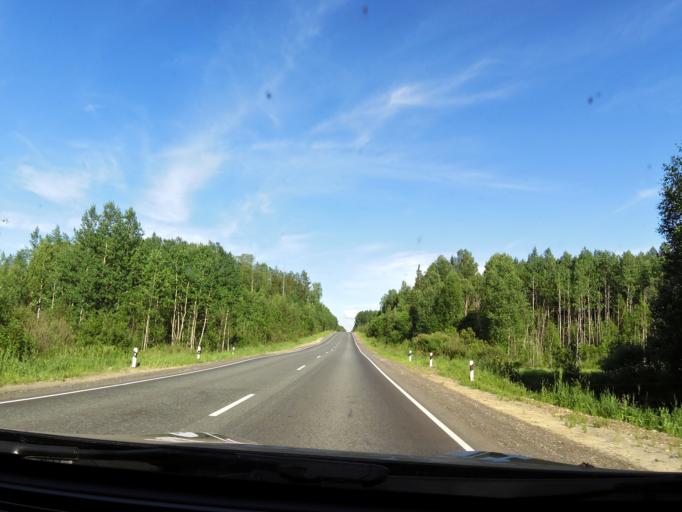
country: RU
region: Kirov
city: Chernaya Kholunitsa
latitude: 58.8722
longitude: 51.5232
